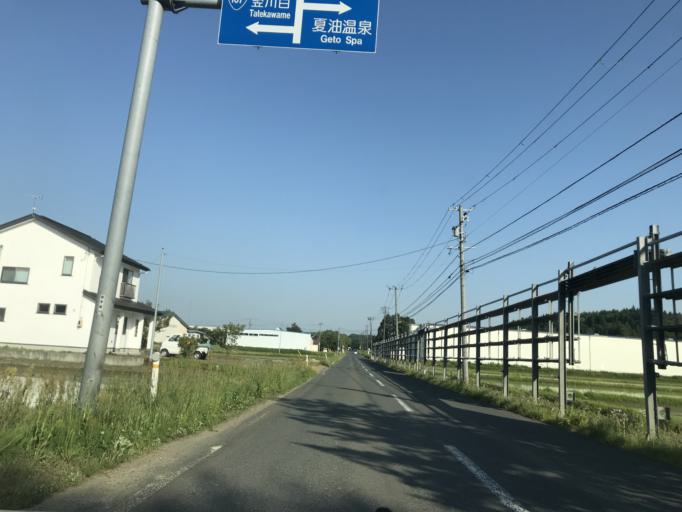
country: JP
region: Iwate
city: Kitakami
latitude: 39.2904
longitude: 140.9975
